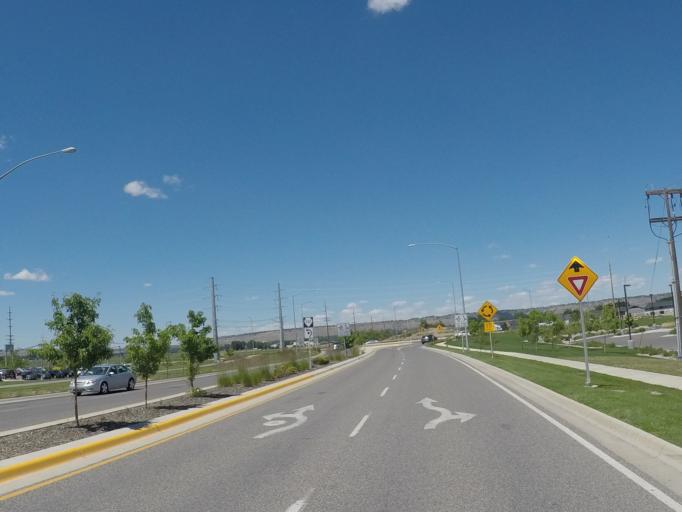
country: US
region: Montana
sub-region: Yellowstone County
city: Billings
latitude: 45.7535
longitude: -108.6174
